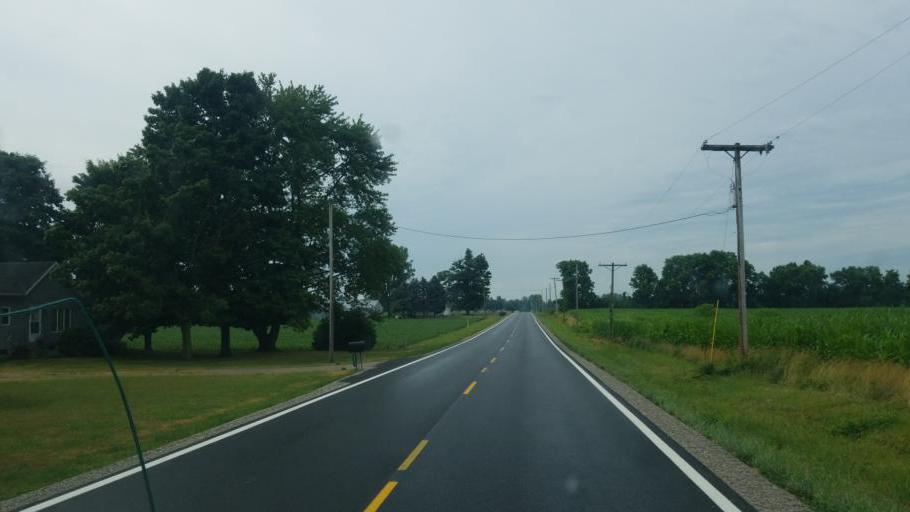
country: US
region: Ohio
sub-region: Defiance County
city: Hicksville
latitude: 41.3619
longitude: -84.6694
